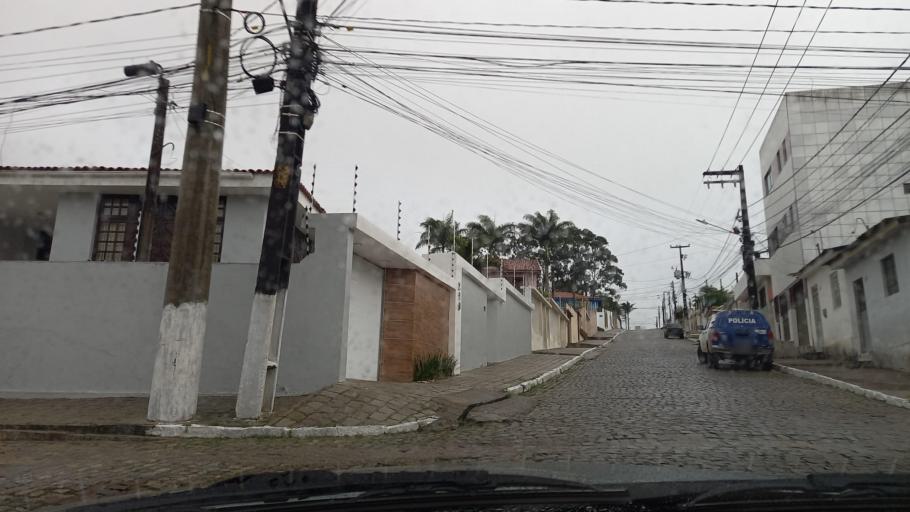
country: BR
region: Pernambuco
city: Garanhuns
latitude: -8.8863
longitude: -36.4949
